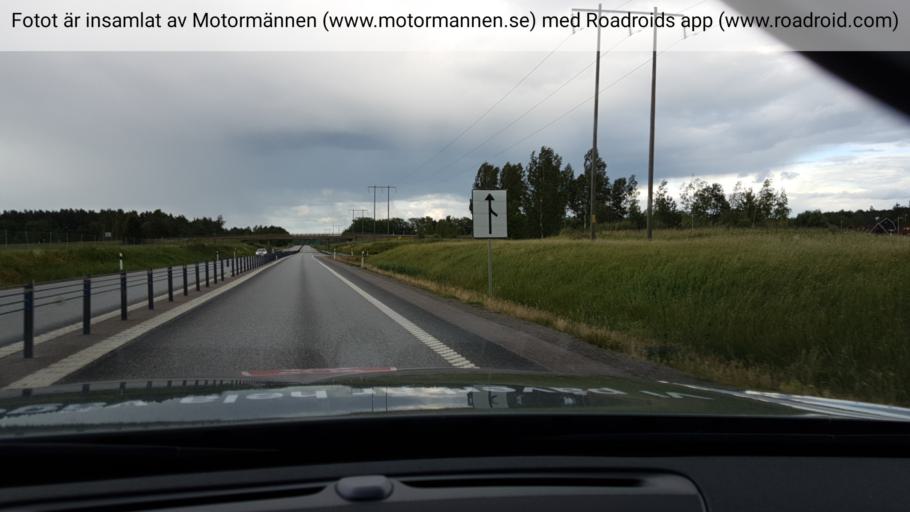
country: SE
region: Vaestmanland
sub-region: Hallstahammars Kommun
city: Hallstahammar
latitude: 59.5877
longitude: 16.2095
